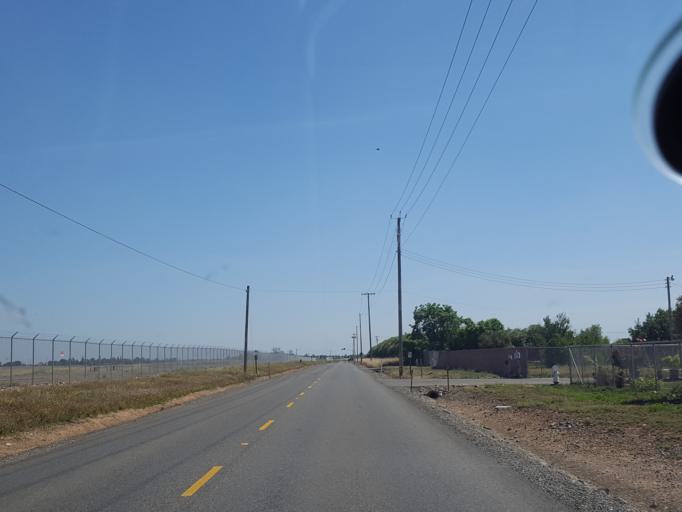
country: US
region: California
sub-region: Sacramento County
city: La Riviera
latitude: 38.5461
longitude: -121.3215
